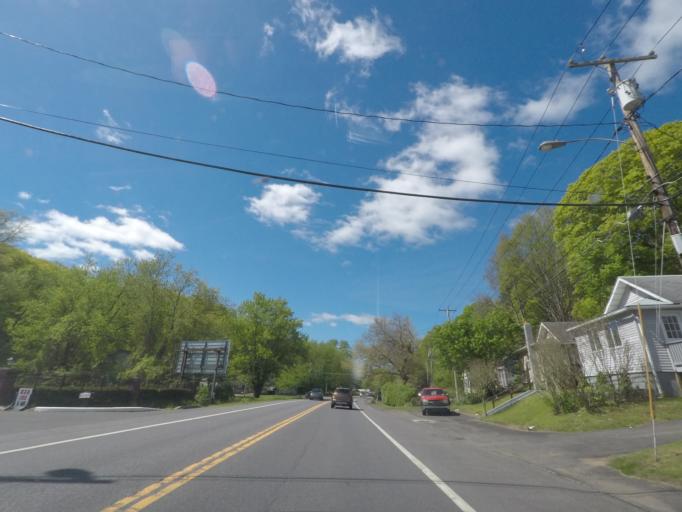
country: US
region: New York
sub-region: Ulster County
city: Glasco
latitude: 42.0425
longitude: -73.9653
